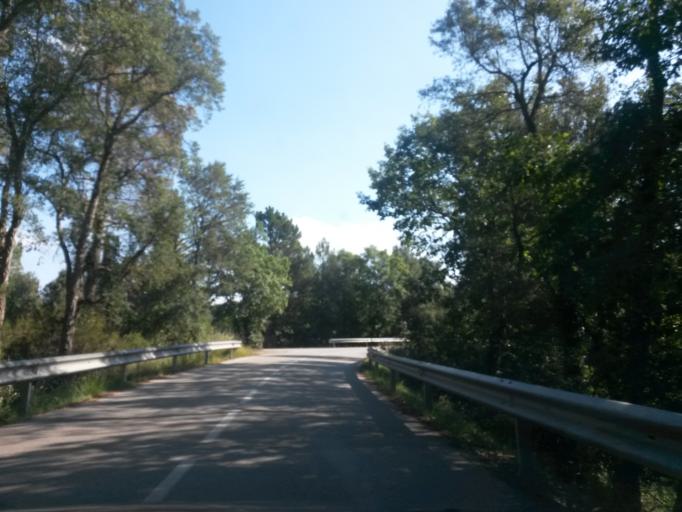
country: ES
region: Catalonia
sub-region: Provincia de Girona
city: Bescano
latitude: 41.9507
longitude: 2.7012
